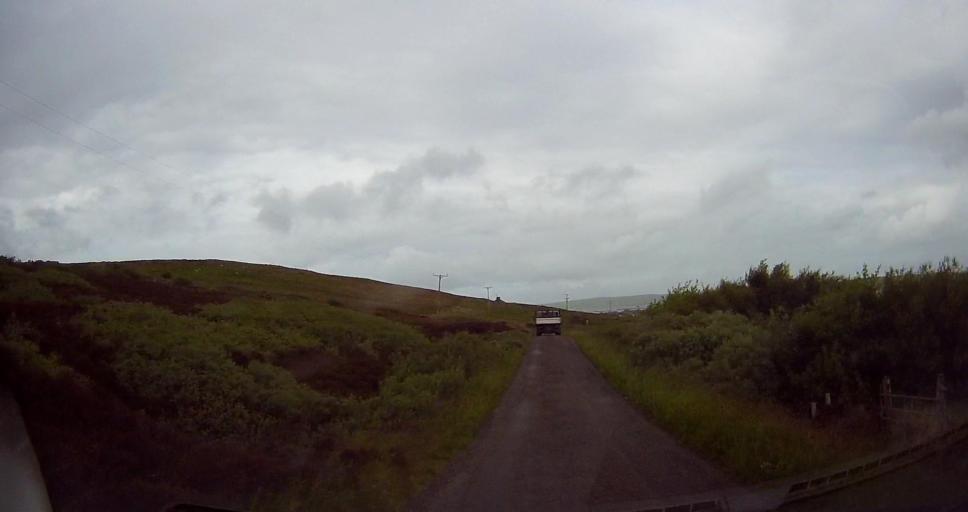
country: GB
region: Scotland
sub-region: Orkney Islands
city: Stromness
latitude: 58.9027
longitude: -3.3163
